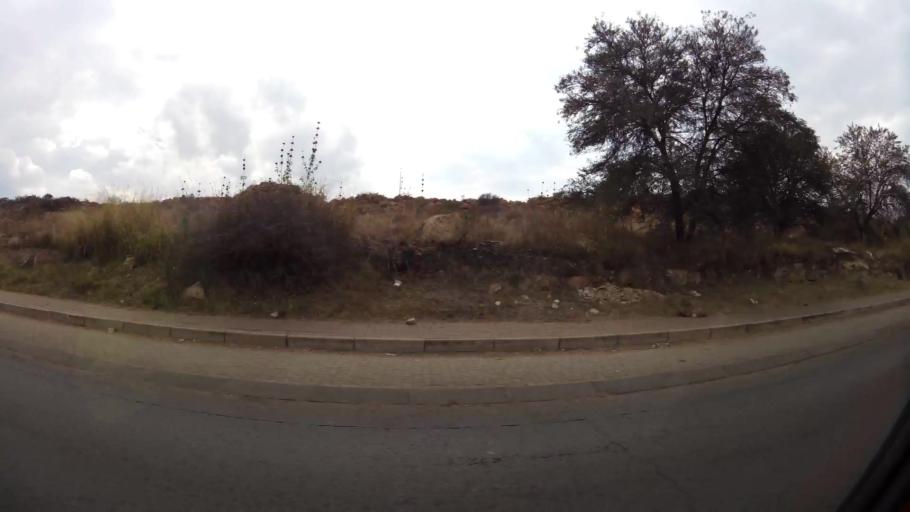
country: ZA
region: Gauteng
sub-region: City of Johannesburg Metropolitan Municipality
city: Soweto
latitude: -26.2340
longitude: 27.8700
